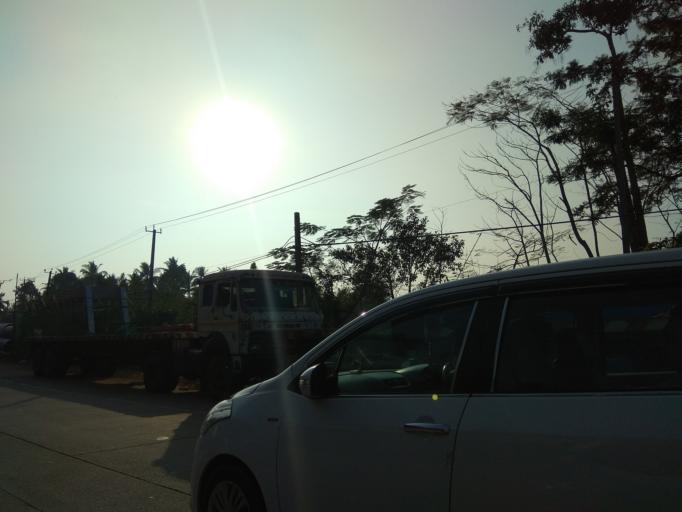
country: IN
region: Karnataka
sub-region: Dakshina Kannada
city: Mangalore
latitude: 12.9137
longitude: 74.8558
